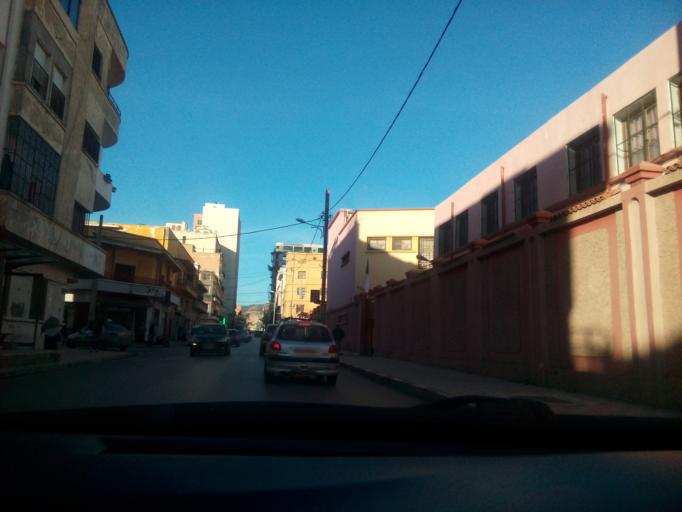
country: DZ
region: Oran
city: Oran
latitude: 35.6871
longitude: -0.6580
